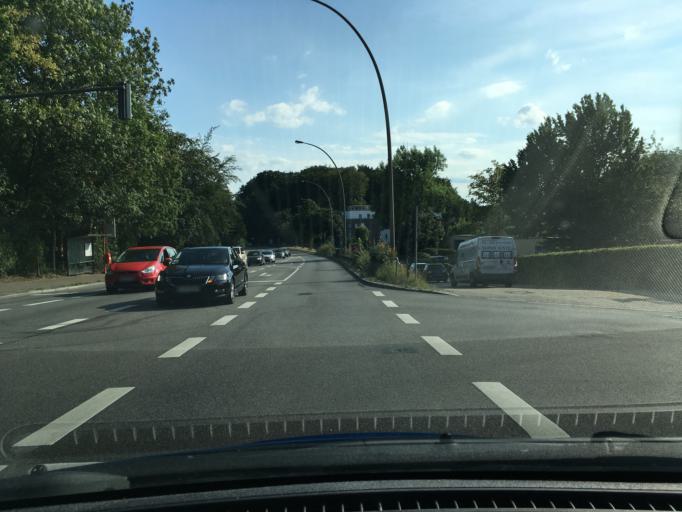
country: DE
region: Hamburg
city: Harburg
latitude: 53.4366
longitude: 9.9856
